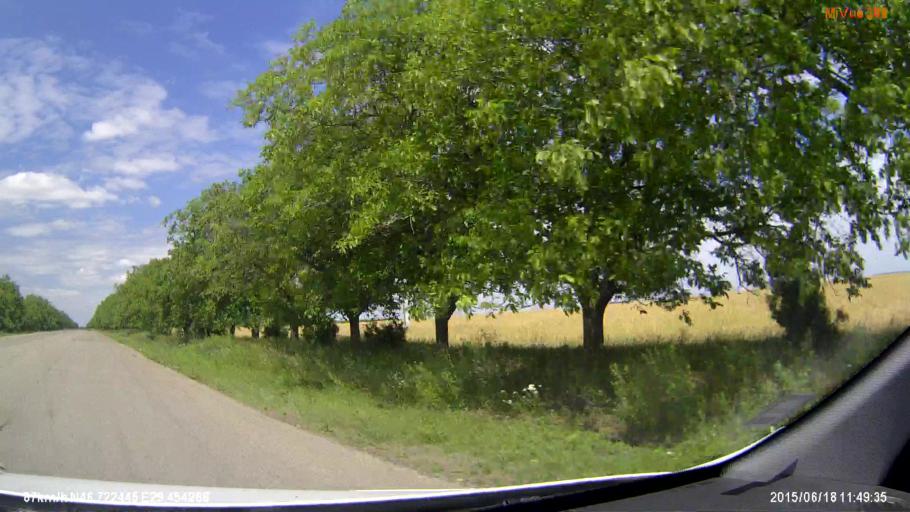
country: MD
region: Causeni
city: Causeni
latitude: 46.7220
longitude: 29.4543
